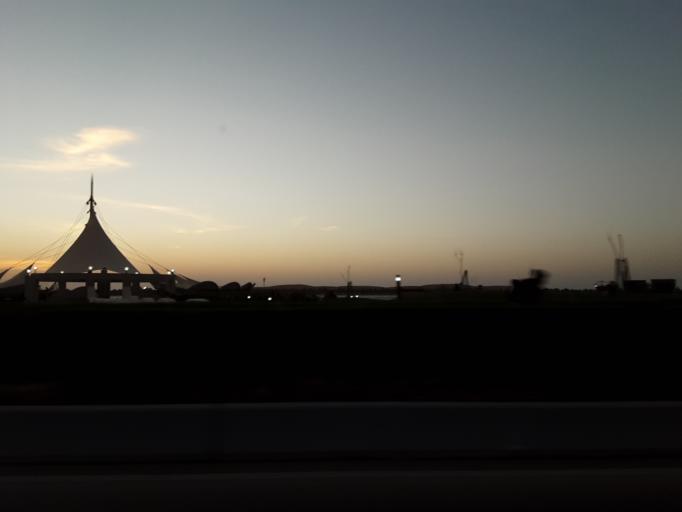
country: AE
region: Abu Dhabi
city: Abu Dhabi
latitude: 24.4953
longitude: 54.3581
